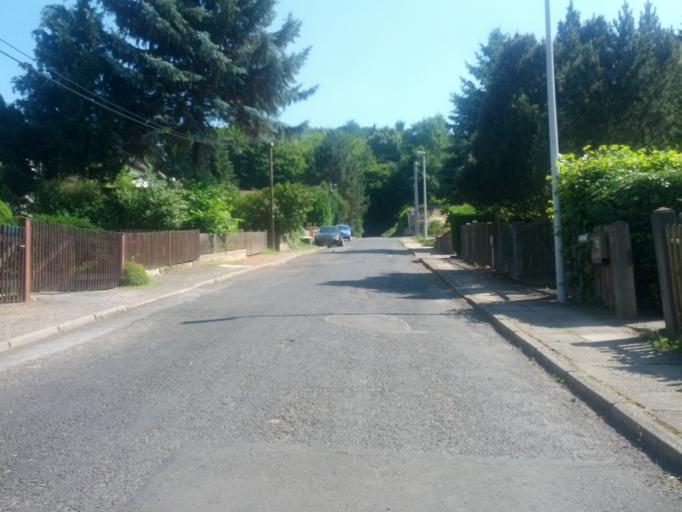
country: DE
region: Thuringia
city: Eisenach
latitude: 50.9775
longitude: 10.2886
